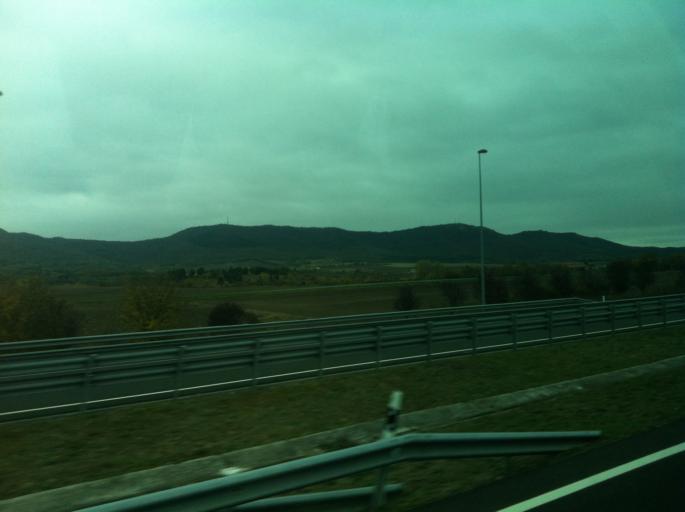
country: ES
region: Basque Country
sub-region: Provincia de Alava
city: Gasteiz / Vitoria
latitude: 42.8273
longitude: -2.7491
